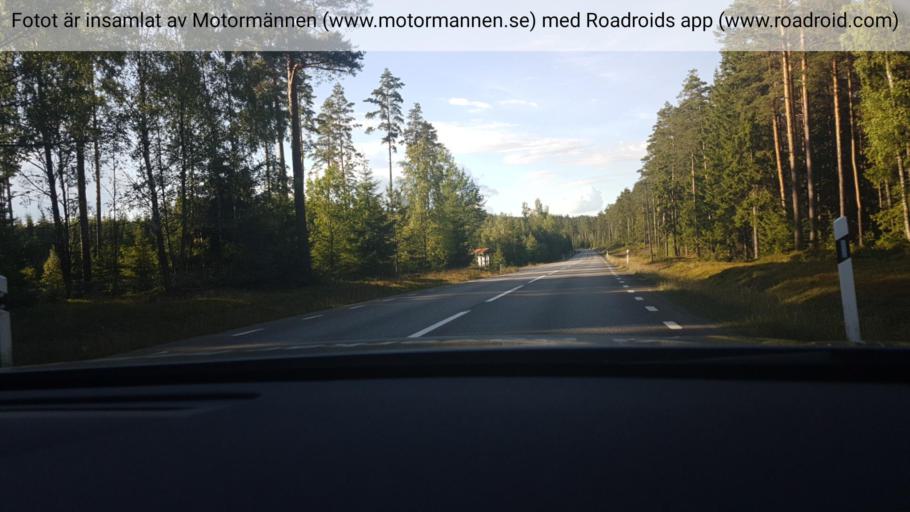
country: SE
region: Joenkoeping
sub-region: Mullsjo Kommun
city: Mullsjoe
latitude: 57.7809
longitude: 13.8340
